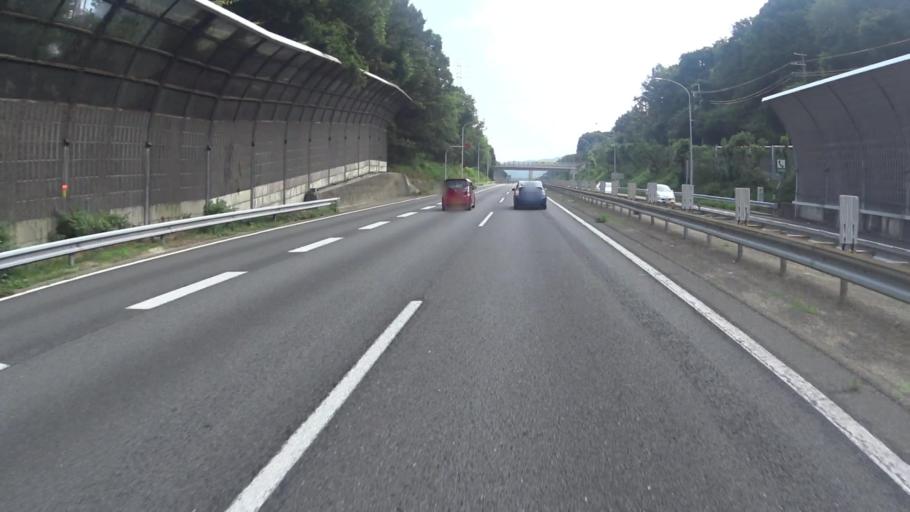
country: JP
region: Shiga Prefecture
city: Otsu-shi
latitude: 34.9749
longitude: 135.8276
